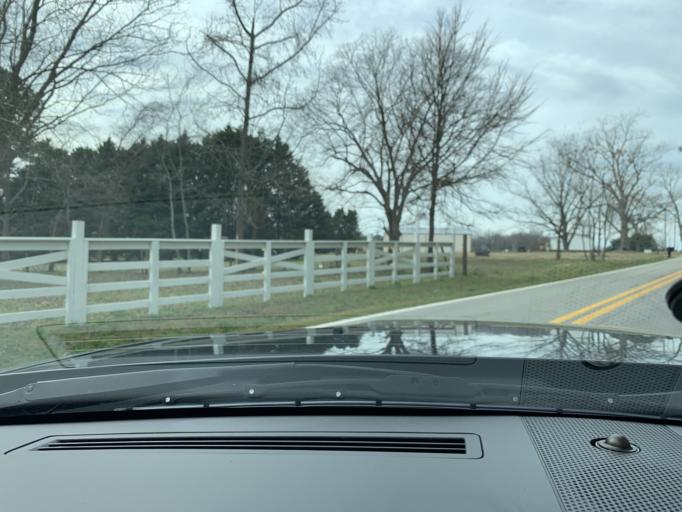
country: US
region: North Carolina
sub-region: Johnston County
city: Wilsons Mills
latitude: 35.6194
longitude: -78.3951
